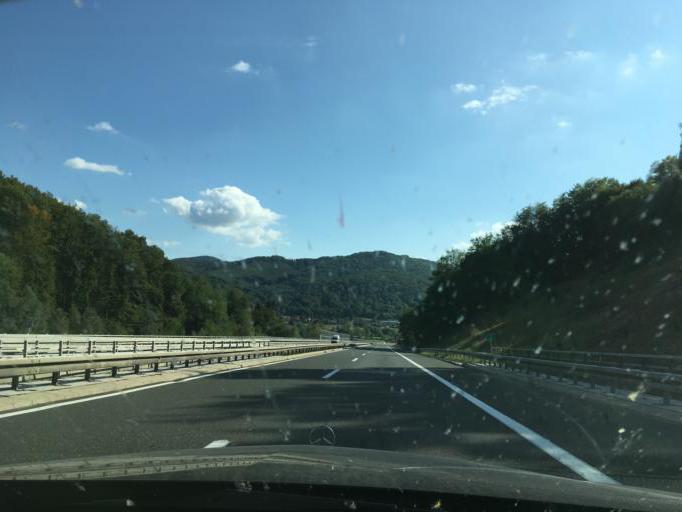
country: HR
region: Varazdinska
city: Ljubescica
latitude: 46.1996
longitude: 16.4111
